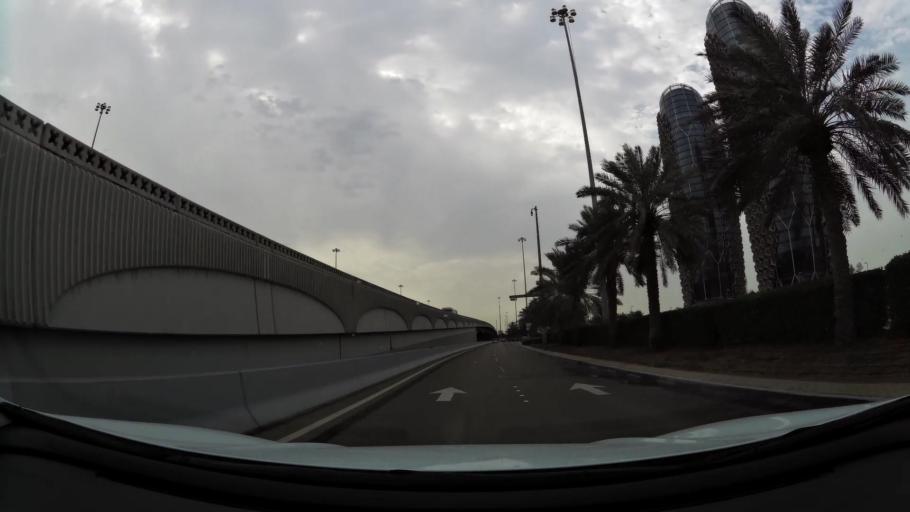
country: AE
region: Abu Dhabi
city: Abu Dhabi
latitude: 24.4582
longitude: 54.4011
